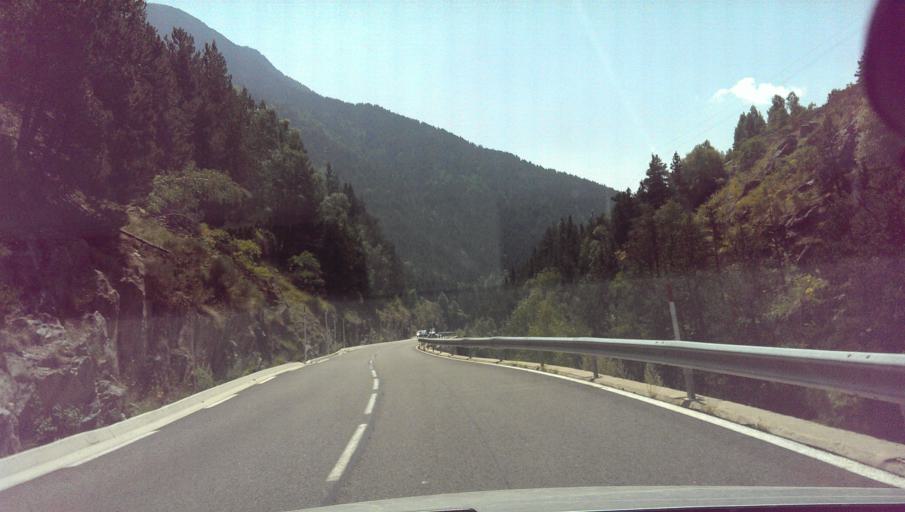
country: AD
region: Encamp
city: Pas de la Casa
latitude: 42.5442
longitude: 1.8263
